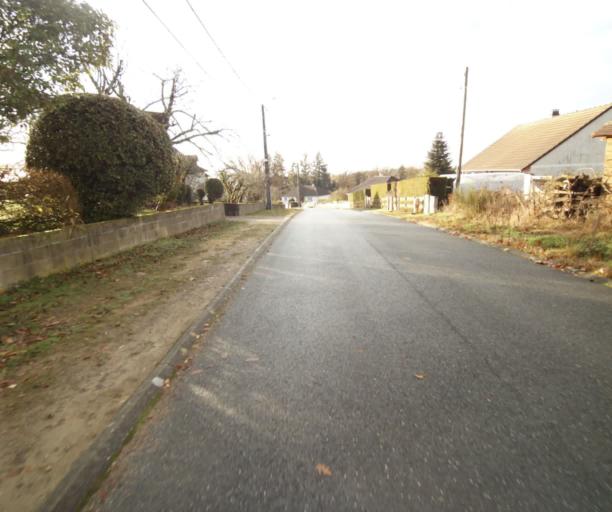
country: FR
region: Limousin
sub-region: Departement de la Correze
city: Saint-Mexant
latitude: 45.2674
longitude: 1.6412
